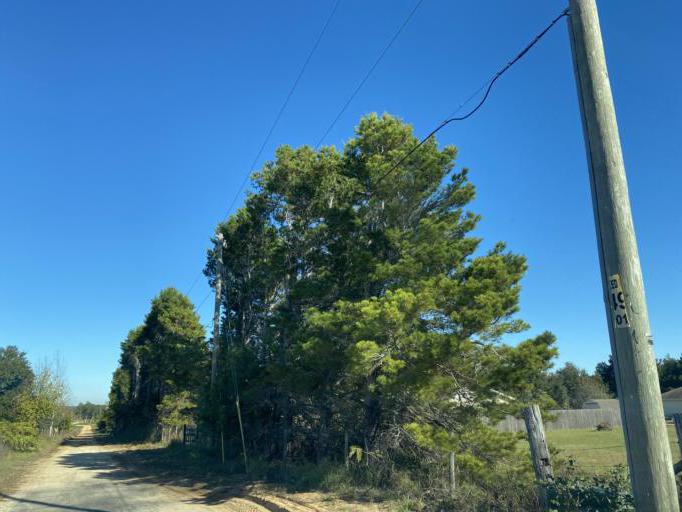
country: US
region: Florida
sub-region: Orange County
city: Oakland
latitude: 28.5251
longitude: -81.6904
